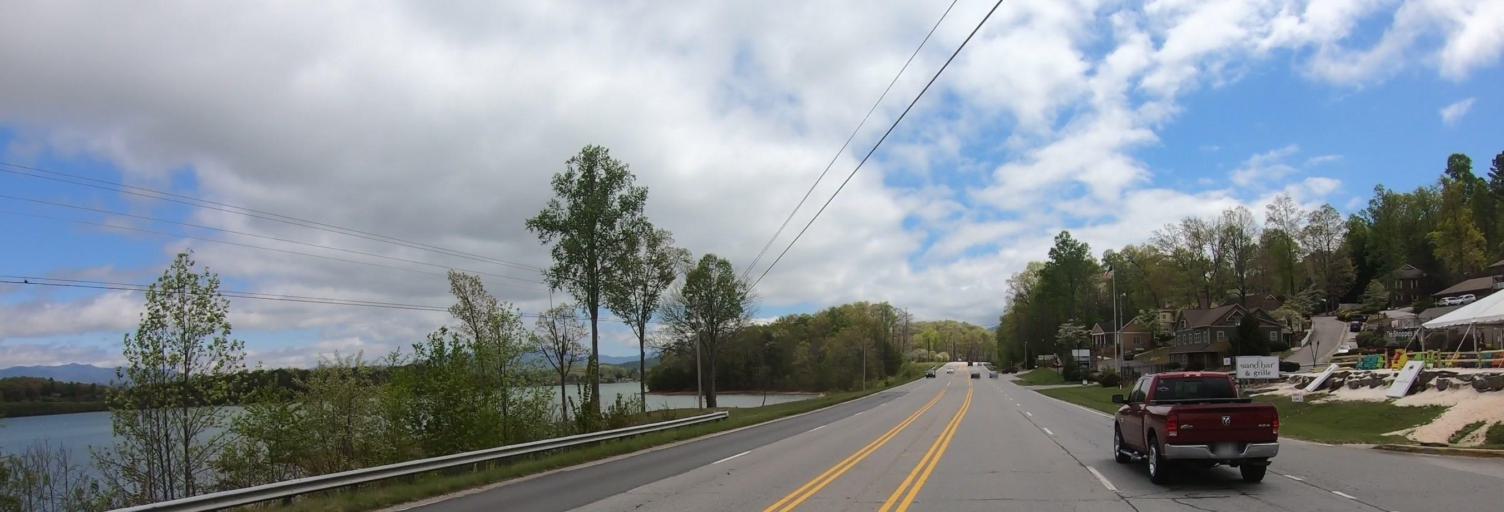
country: US
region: Georgia
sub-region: Towns County
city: Hiawassee
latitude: 34.9675
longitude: -83.8151
